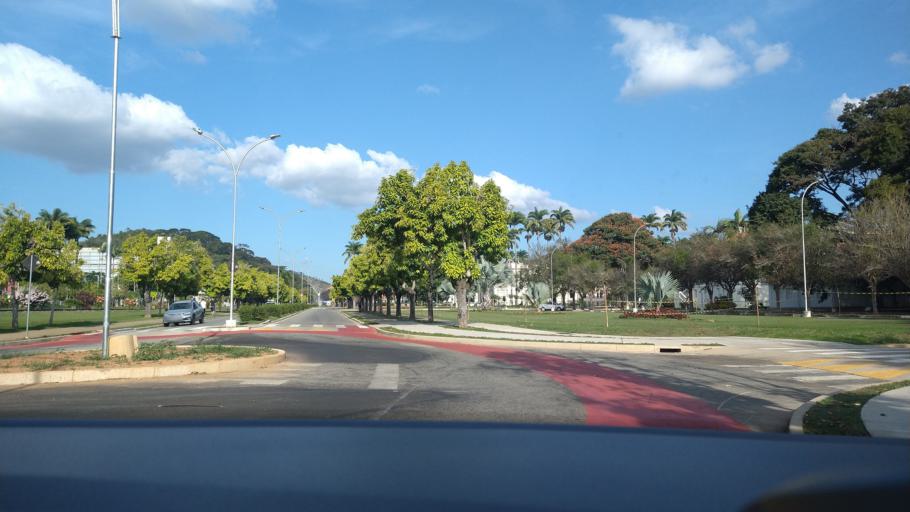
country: BR
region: Minas Gerais
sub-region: Vicosa
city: Vicosa
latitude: -20.7600
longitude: -42.8705
